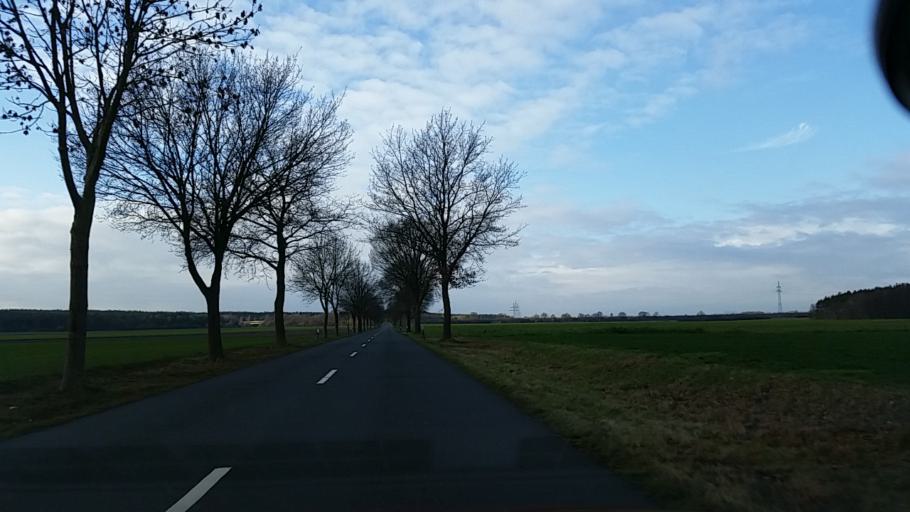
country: DE
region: Lower Saxony
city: Wieren
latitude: 52.8875
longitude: 10.6484
